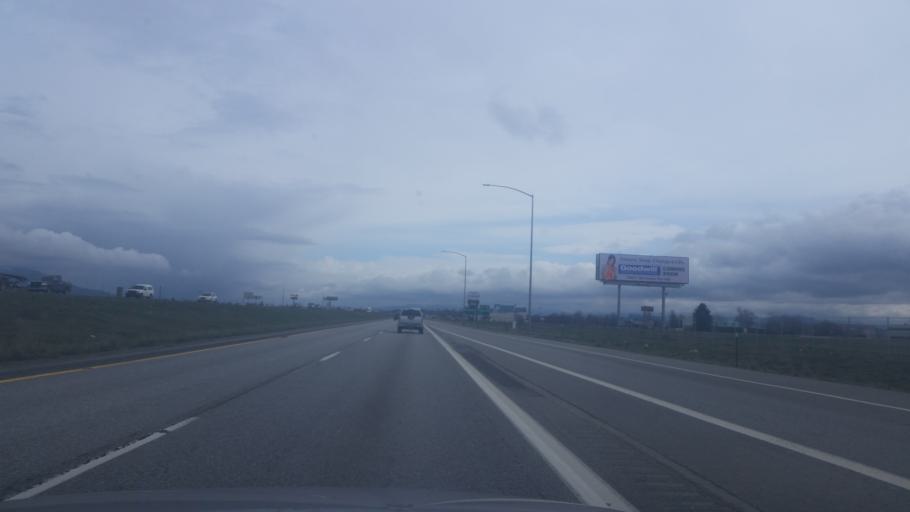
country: US
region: Washington
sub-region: Spokane County
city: Otis Orchards-East Farms
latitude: 47.7031
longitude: -117.0152
